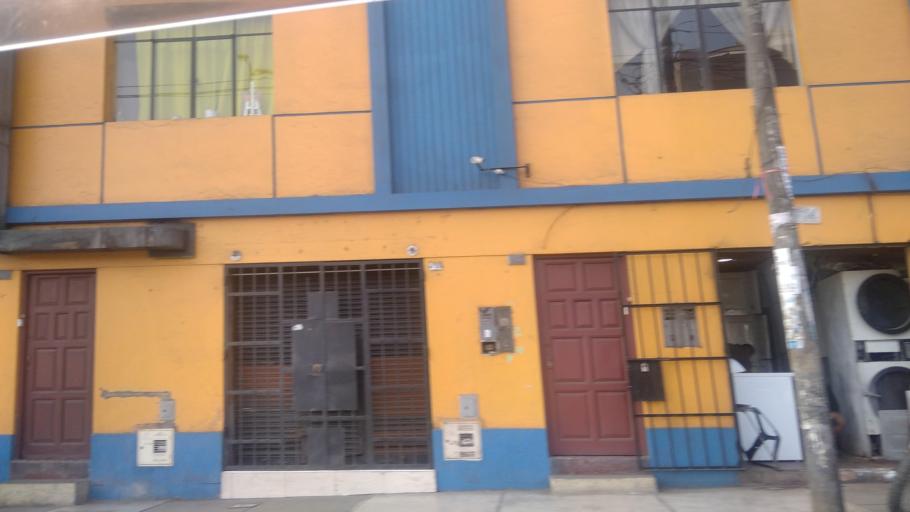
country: PE
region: Lima
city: Lima
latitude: -12.0339
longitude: -77.0518
